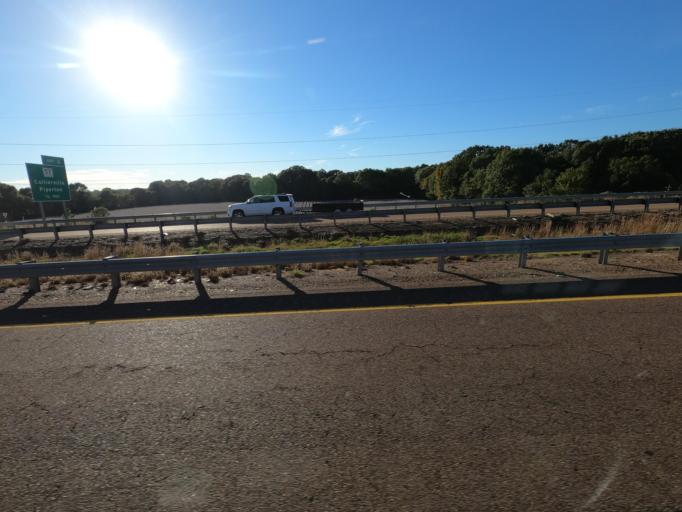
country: US
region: Tennessee
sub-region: Fayette County
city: Piperton
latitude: 35.0569
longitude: -89.6374
